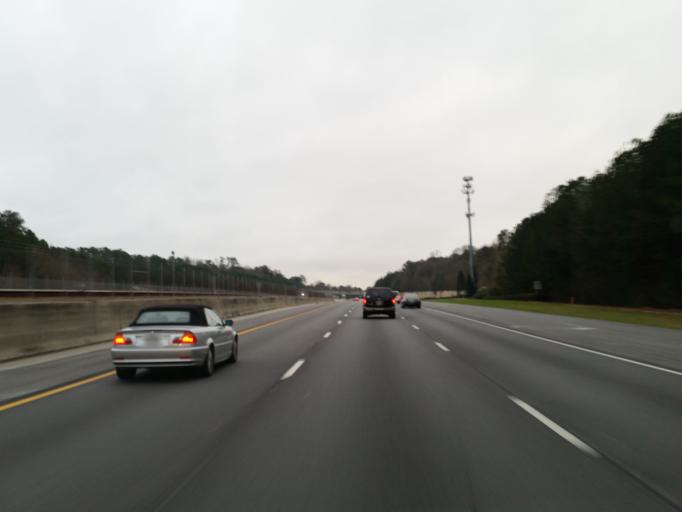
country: US
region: Georgia
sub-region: DeKalb County
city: North Atlanta
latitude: 33.8797
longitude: -84.3650
